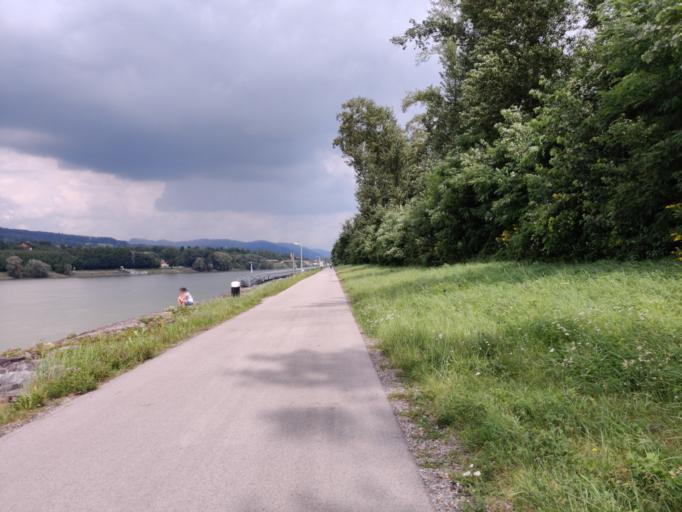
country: AT
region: Lower Austria
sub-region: Politischer Bezirk Melk
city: Melk
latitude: 48.2298
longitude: 15.3221
